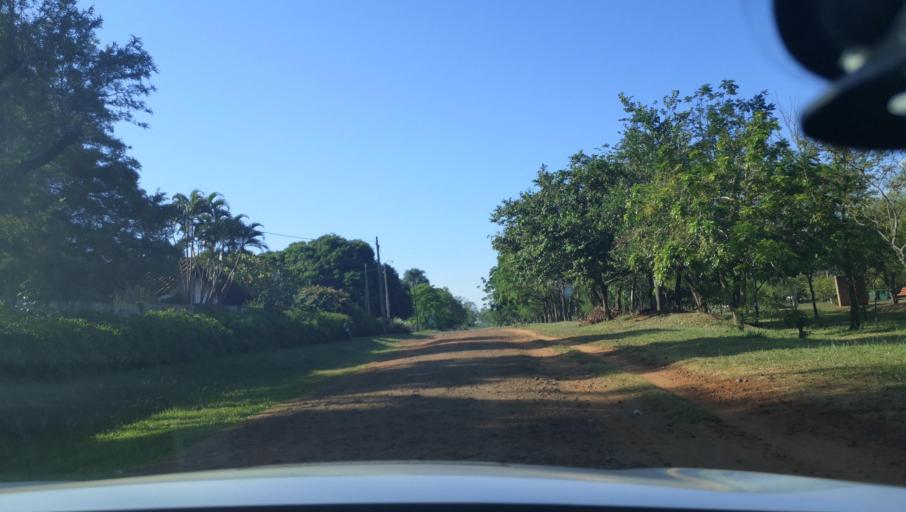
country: PY
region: Itapua
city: Carmen del Parana
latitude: -27.1639
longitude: -56.2399
